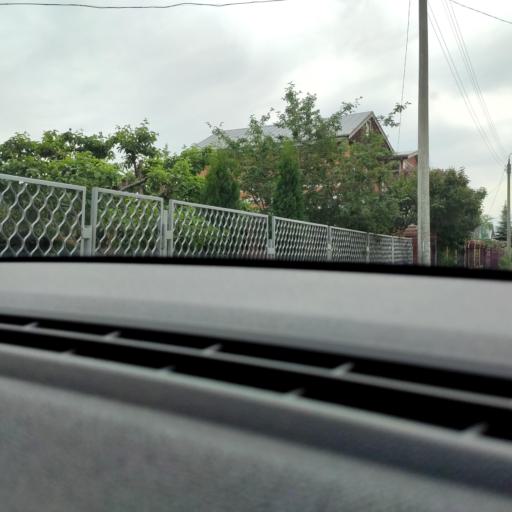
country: RU
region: Samara
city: Podstepki
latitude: 53.5063
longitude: 49.1609
